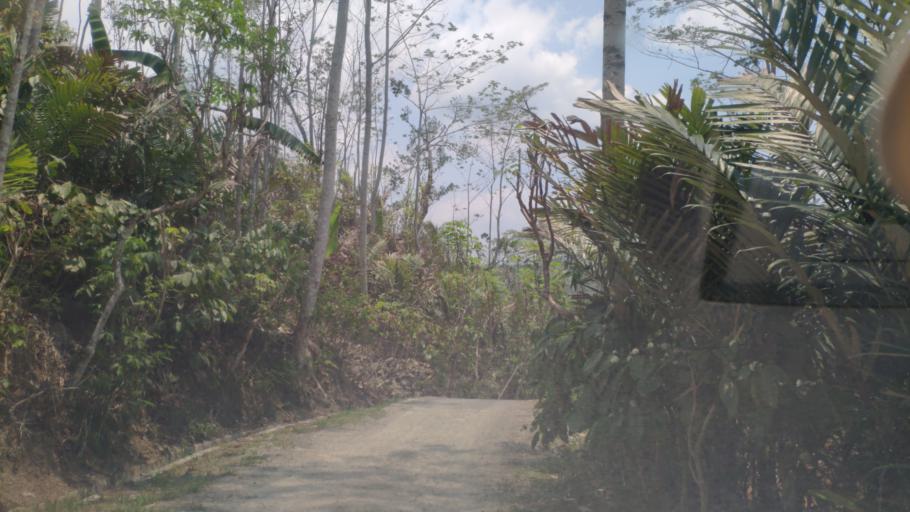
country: ID
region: Central Java
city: Wonosobo
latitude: -7.3151
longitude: 109.7439
